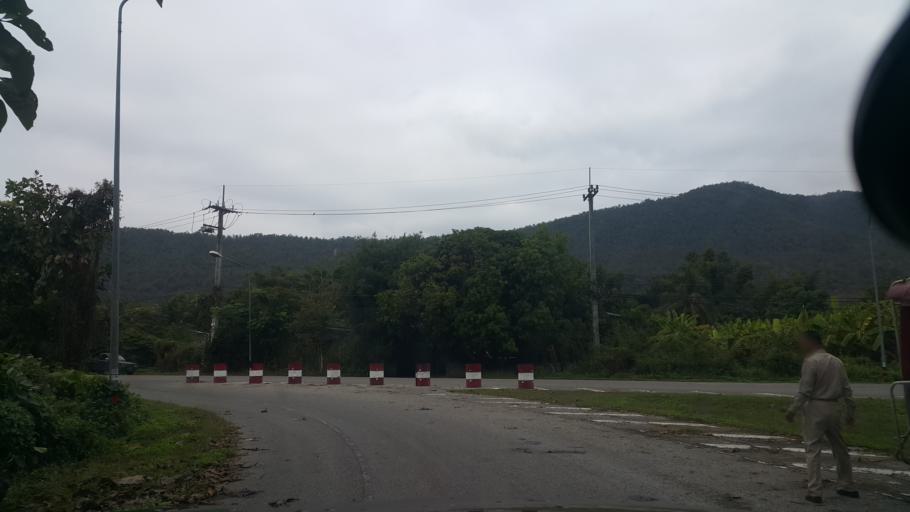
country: TH
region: Chiang Mai
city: Mae On
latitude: 18.7424
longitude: 99.2037
